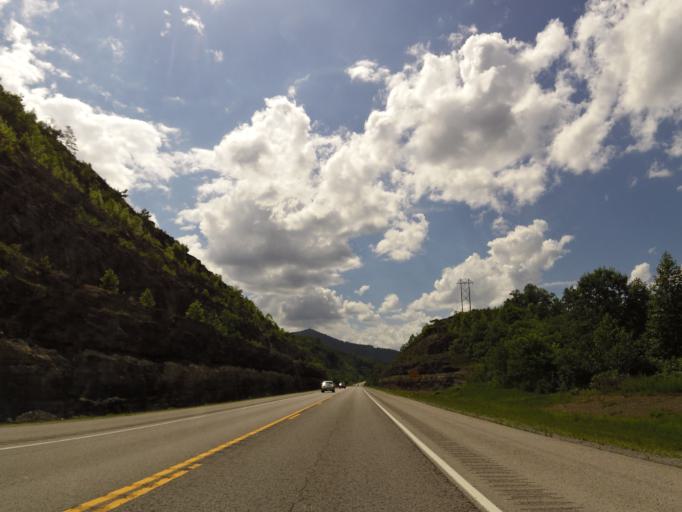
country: US
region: Kentucky
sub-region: Harlan County
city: Harlan
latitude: 36.7809
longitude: -83.2304
